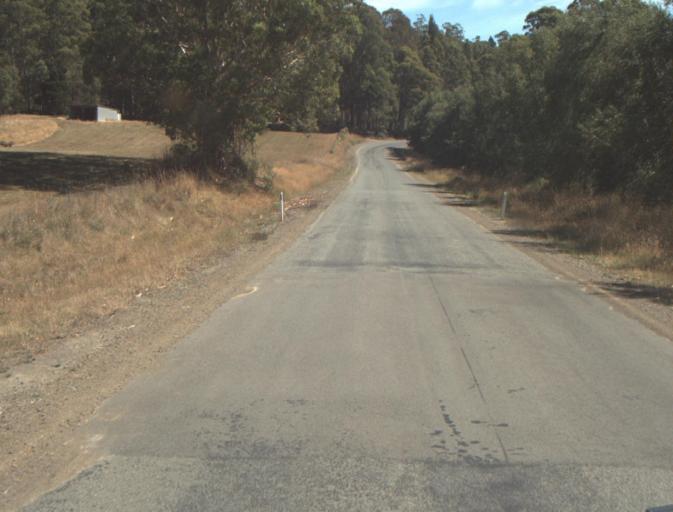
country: AU
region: Tasmania
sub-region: Dorset
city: Scottsdale
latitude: -41.3118
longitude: 147.3897
